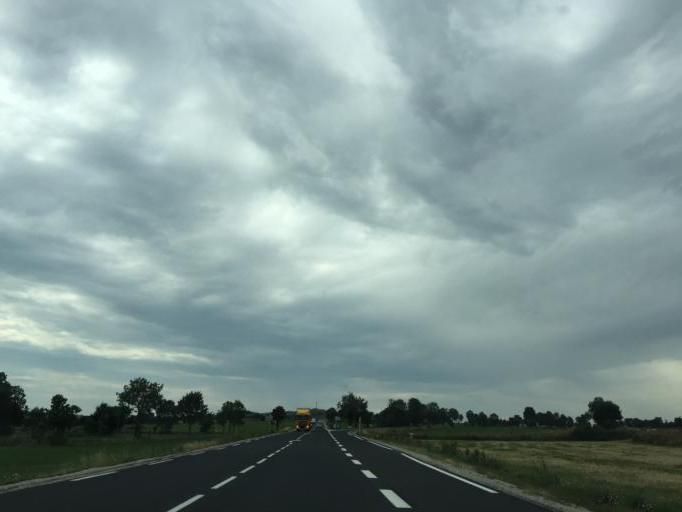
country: FR
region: Auvergne
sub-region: Departement de la Haute-Loire
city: Solignac-sur-Loire
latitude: 44.8655
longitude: 3.8485
